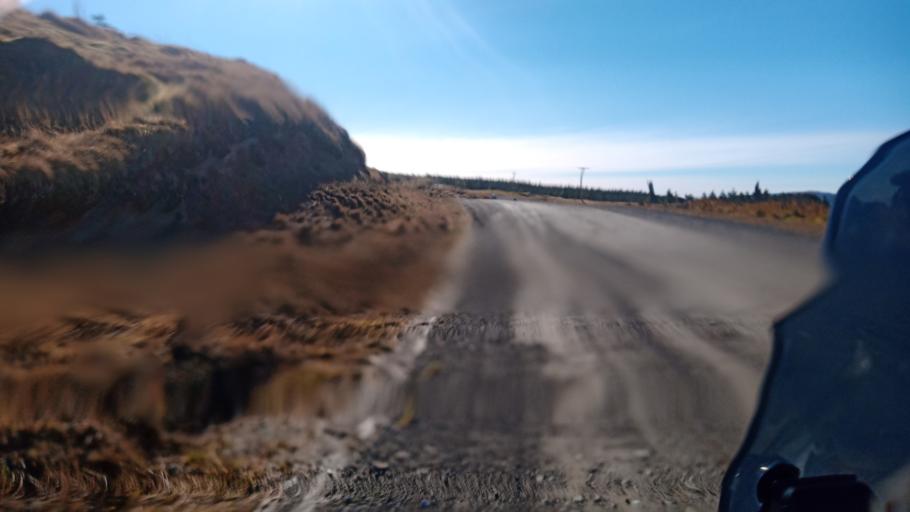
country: NZ
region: Gisborne
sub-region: Gisborne District
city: Gisborne
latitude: -38.1920
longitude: 177.8157
